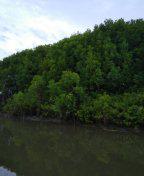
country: IN
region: Kerala
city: Chavakkad
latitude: 10.5381
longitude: 76.0494
